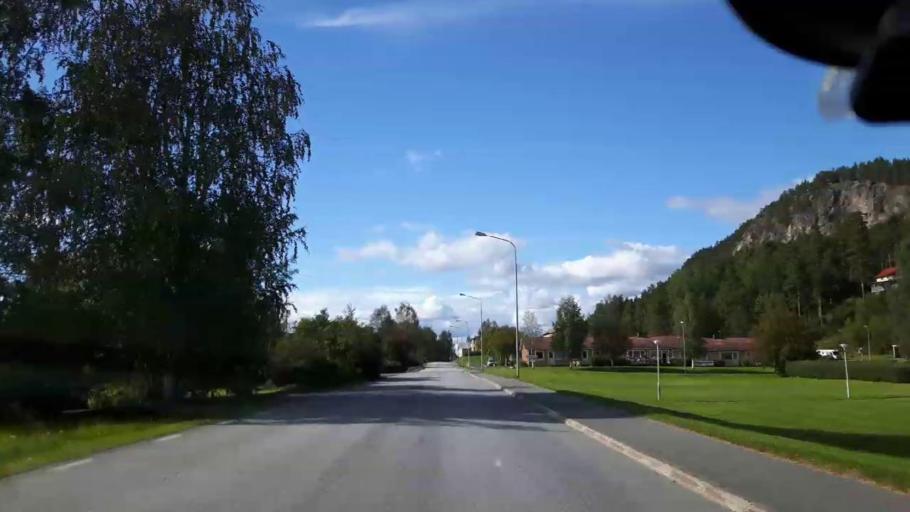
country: SE
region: Jaemtland
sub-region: Braecke Kommun
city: Braecke
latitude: 63.1684
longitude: 15.5840
